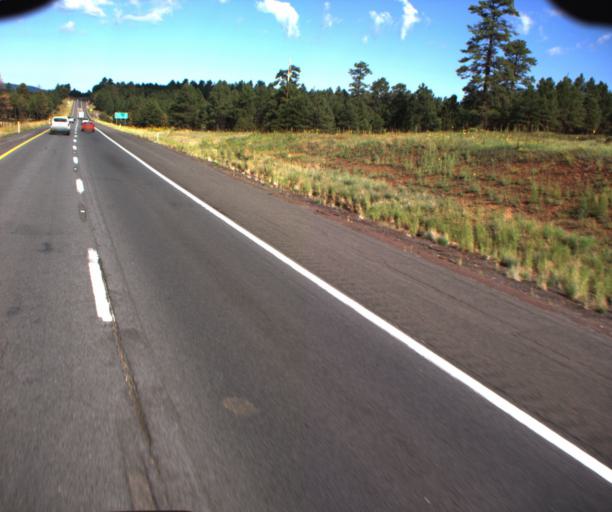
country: US
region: Arizona
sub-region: Coconino County
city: Flagstaff
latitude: 35.2002
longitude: -111.7551
